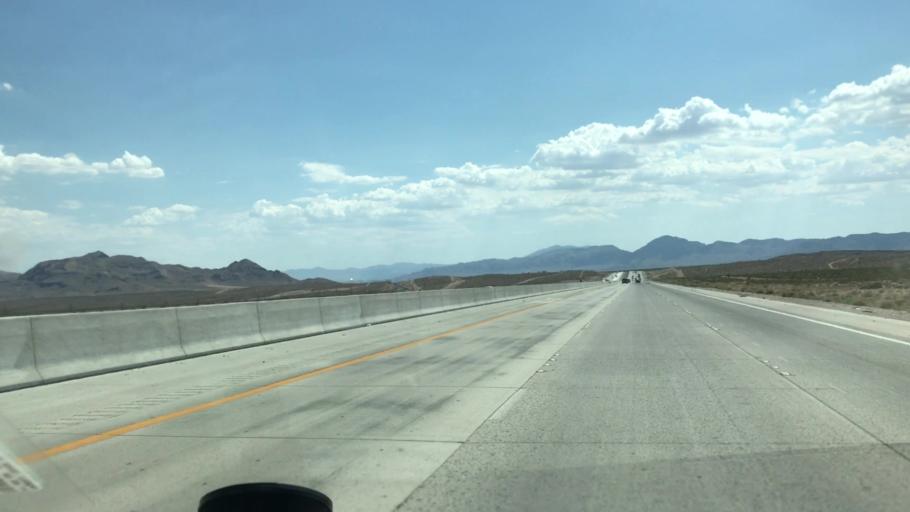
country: US
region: Nevada
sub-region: Clark County
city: Enterprise
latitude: 35.8390
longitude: -115.2799
